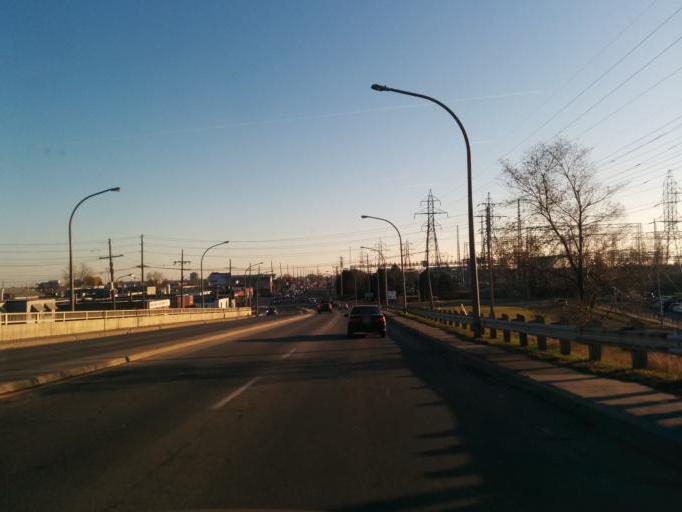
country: CA
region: Ontario
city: Etobicoke
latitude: 43.6374
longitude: -79.5338
